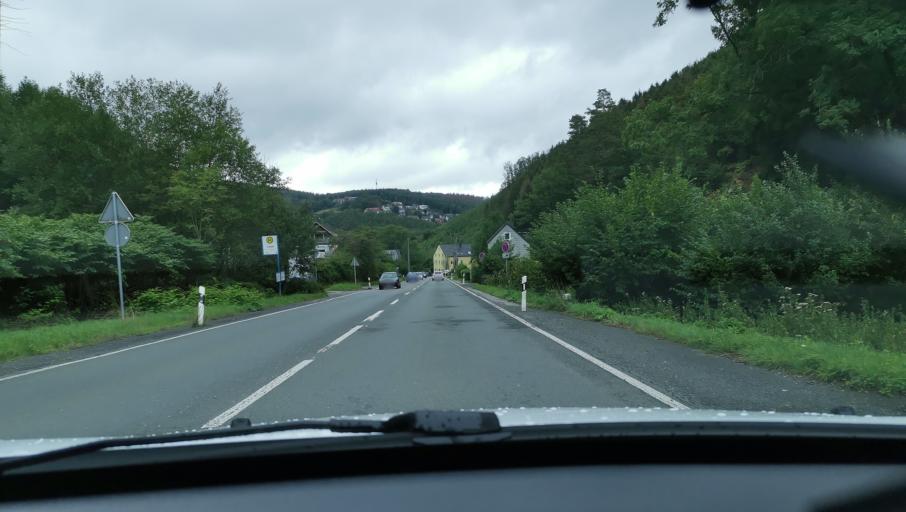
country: DE
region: North Rhine-Westphalia
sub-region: Regierungsbezirk Arnsberg
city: Hagen
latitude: 51.3268
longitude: 7.4664
